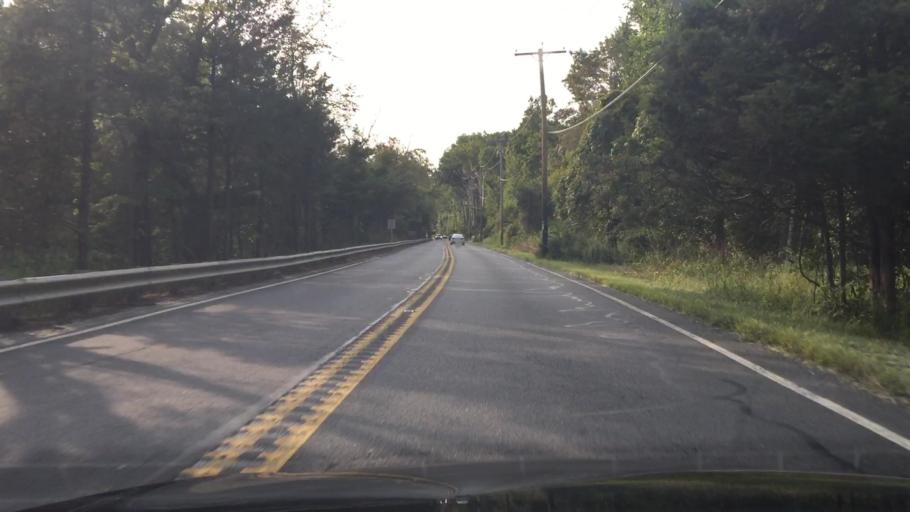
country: US
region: New Jersey
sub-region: Hunterdon County
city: Lambertville
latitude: 40.3150
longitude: -74.8919
